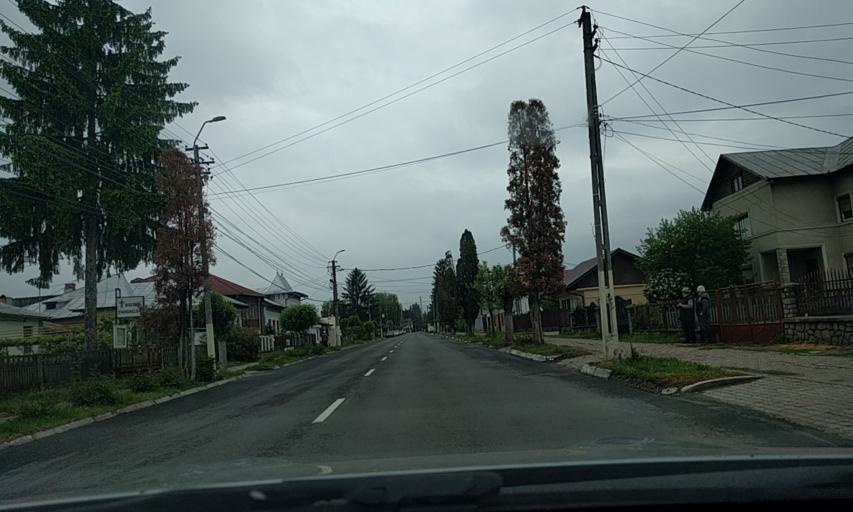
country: RO
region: Dambovita
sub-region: Oras Pucioasa
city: Pucioasa
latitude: 45.0675
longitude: 25.4367
